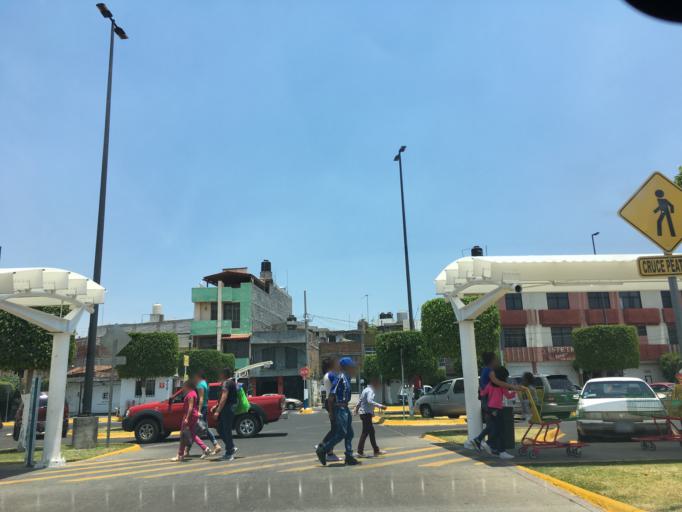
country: MX
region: Guanajuato
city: Uriangato
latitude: 20.1354
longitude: -101.1835
